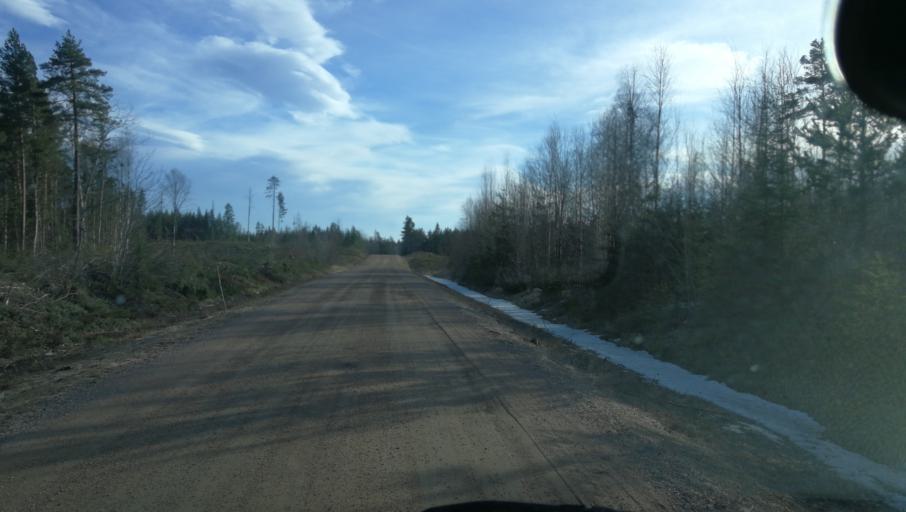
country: SE
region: Dalarna
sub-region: Vansbro Kommun
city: Vansbro
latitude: 60.8265
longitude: 14.1942
